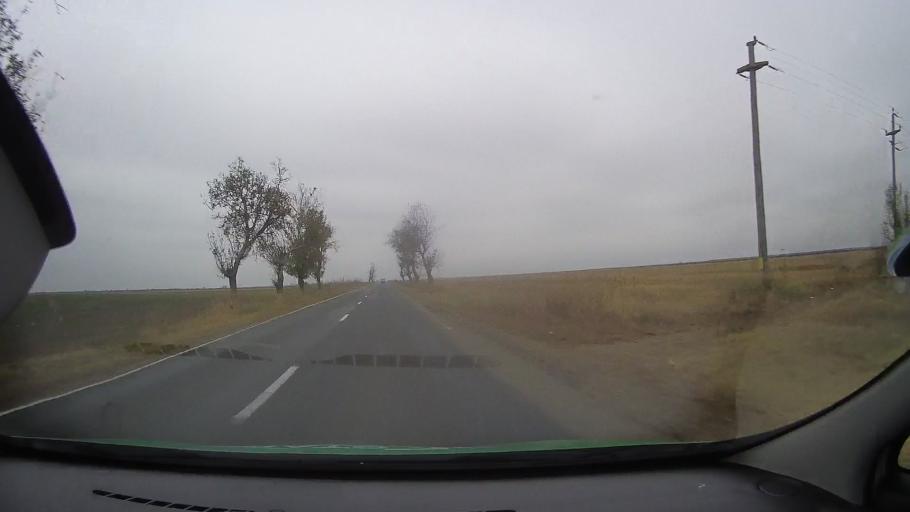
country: RO
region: Ialomita
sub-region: Comuna Scanteia
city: Scanteia
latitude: 44.7660
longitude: 27.4678
